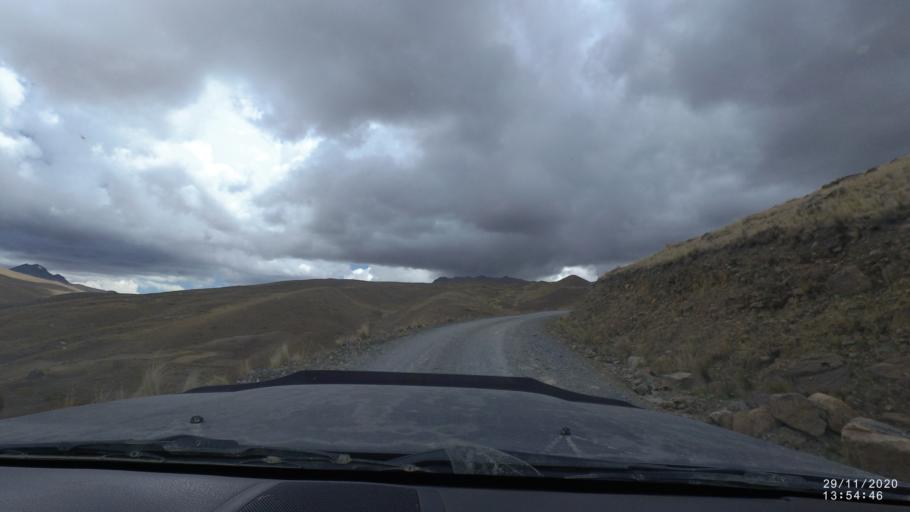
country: BO
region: Cochabamba
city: Sipe Sipe
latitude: -17.1750
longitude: -66.3546
